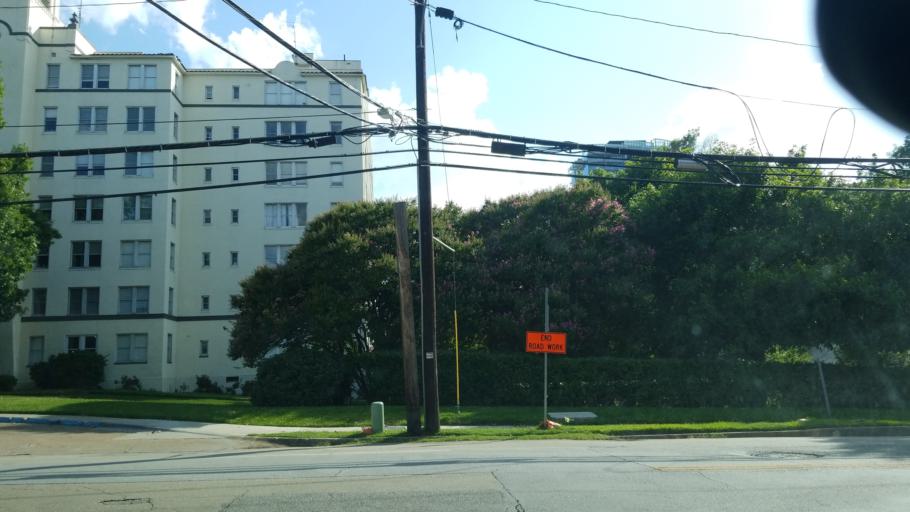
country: US
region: Texas
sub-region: Dallas County
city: Dallas
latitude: 32.7987
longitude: -96.8080
